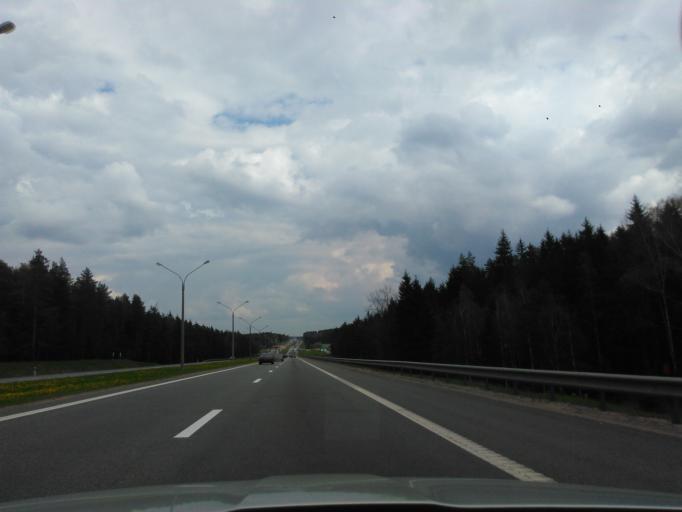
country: BY
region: Minsk
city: Kalodzishchy
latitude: 53.9716
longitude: 27.7557
